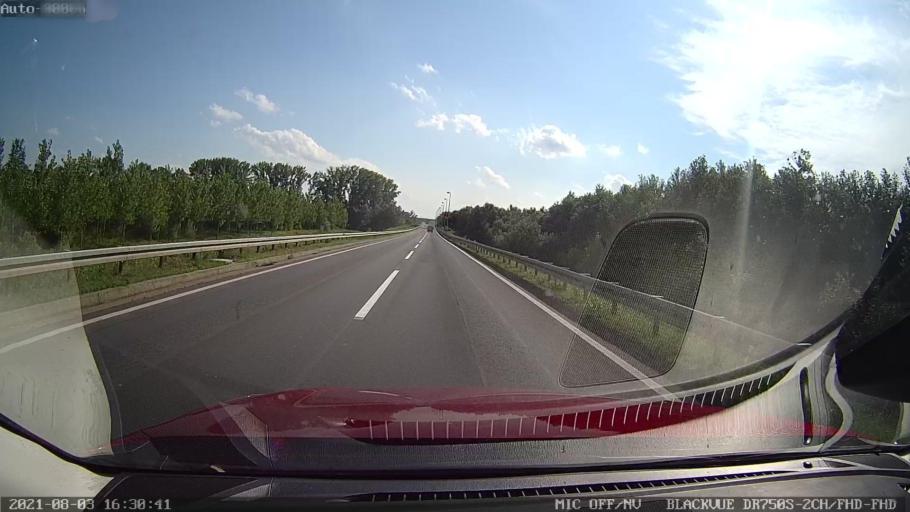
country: HR
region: Osjecko-Baranjska
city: Visnjevac
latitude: 45.5803
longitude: 18.6432
